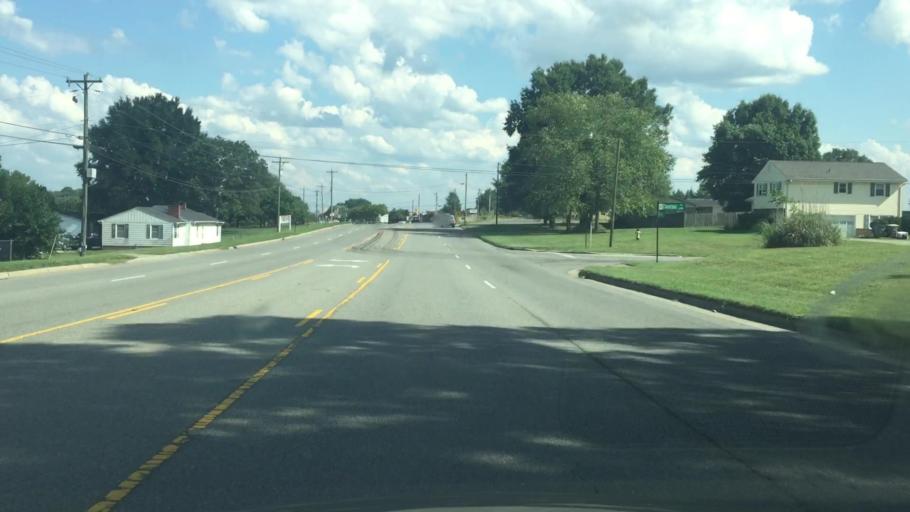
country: US
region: North Carolina
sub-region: Cabarrus County
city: Kannapolis
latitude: 35.4248
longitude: -80.6782
